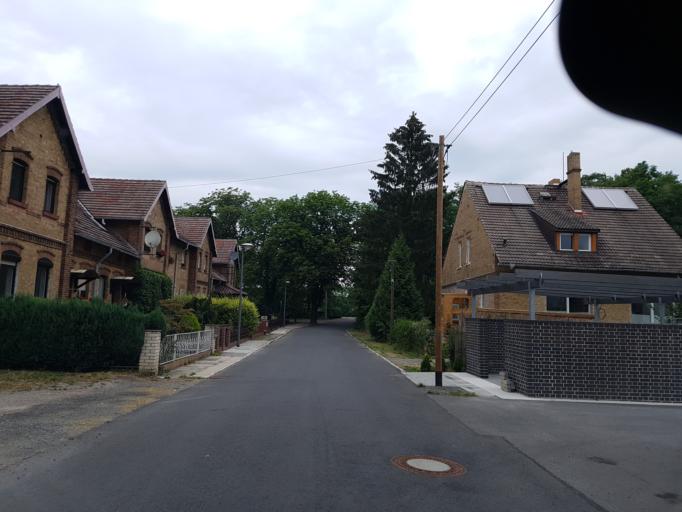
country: DE
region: Brandenburg
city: Sallgast
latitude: 51.5624
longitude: 13.8849
